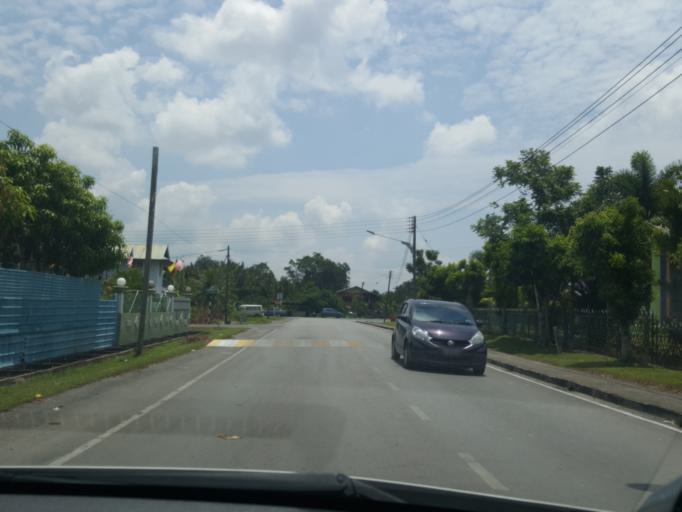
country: MY
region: Sarawak
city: Sarikei
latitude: 2.1266
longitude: 111.5167
